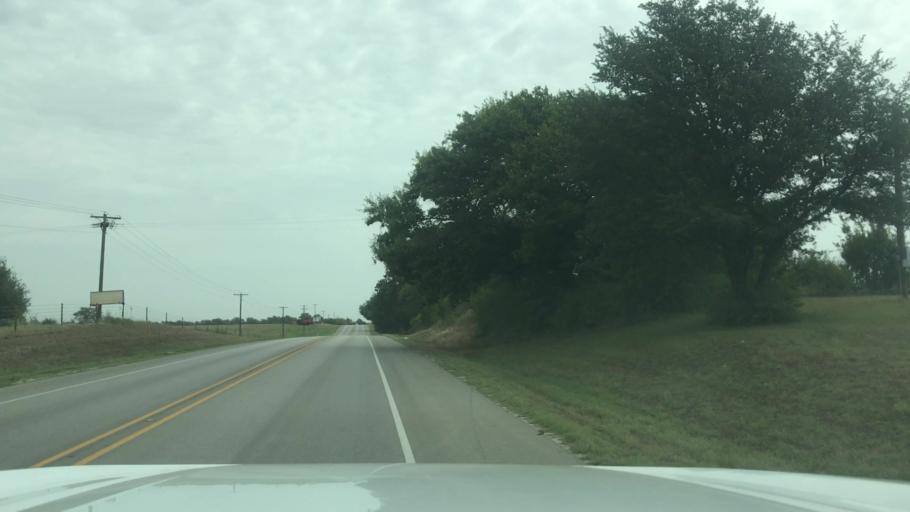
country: US
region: Texas
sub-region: Erath County
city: Dublin
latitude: 32.0923
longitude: -98.4172
